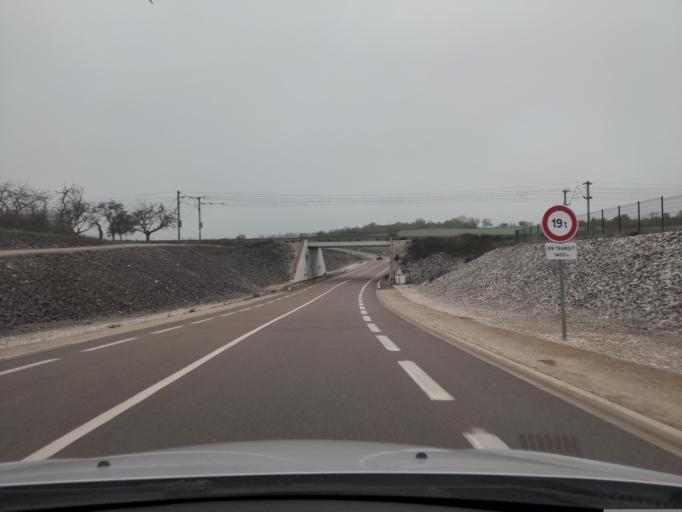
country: FR
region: Bourgogne
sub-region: Departement de la Cote-d'Or
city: Ruffey-les-Echirey
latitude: 47.3656
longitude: 5.0729
